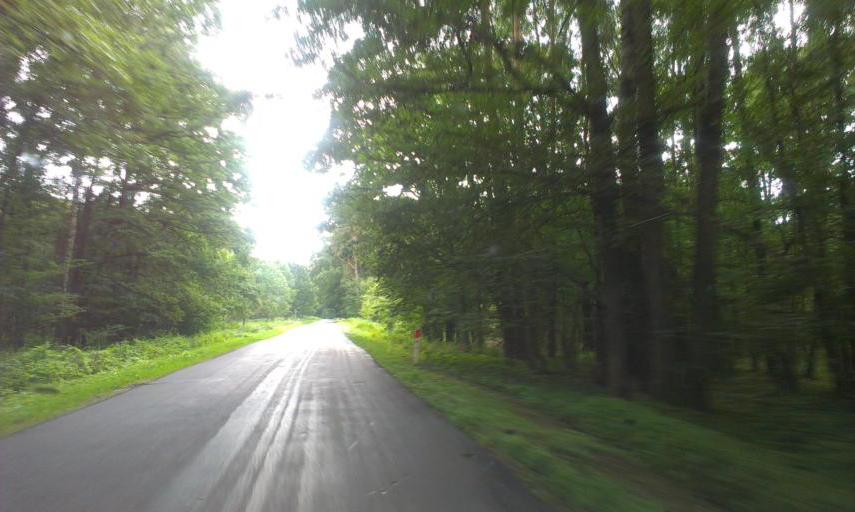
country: PL
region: West Pomeranian Voivodeship
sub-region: Powiat swidwinski
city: Polczyn-Zdroj
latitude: 53.8392
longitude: 16.1553
